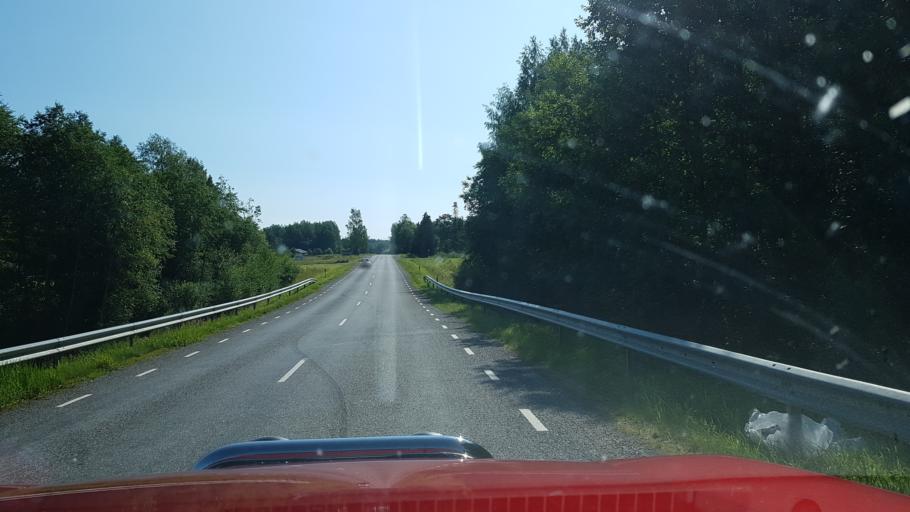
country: EE
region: Vorumaa
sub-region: Voru linn
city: Voru
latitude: 57.9740
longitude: 26.8318
